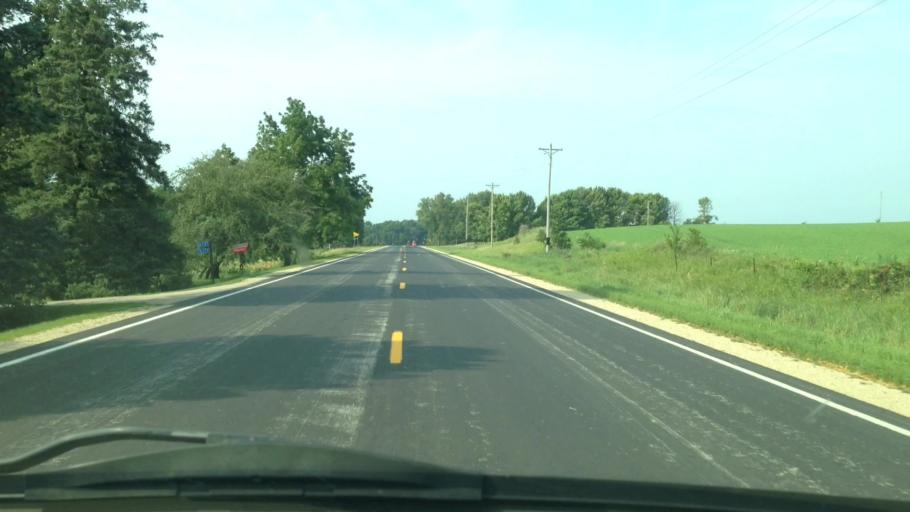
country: US
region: Minnesota
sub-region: Winona County
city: Lewiston
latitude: 43.9604
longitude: -91.9543
